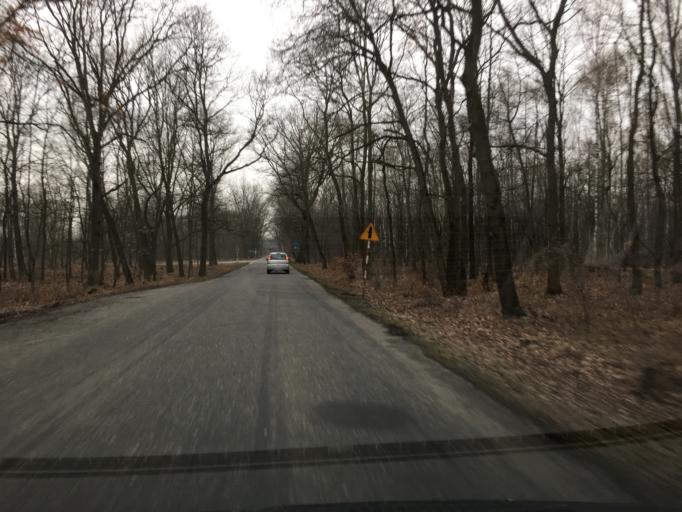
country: PL
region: Opole Voivodeship
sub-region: Powiat kedzierzynsko-kozielski
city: Kedzierzyn-Kozle
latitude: 50.3213
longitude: 18.2357
